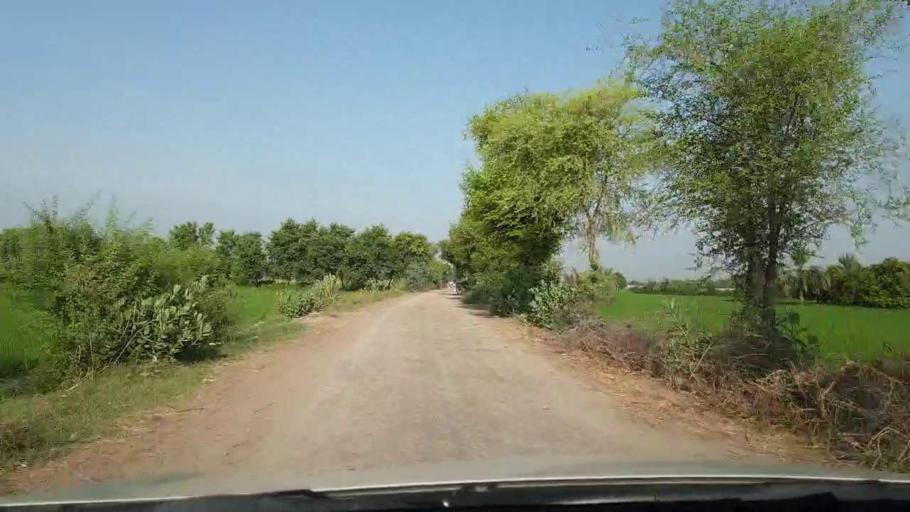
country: PK
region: Sindh
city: Larkana
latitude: 27.5452
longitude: 68.2643
